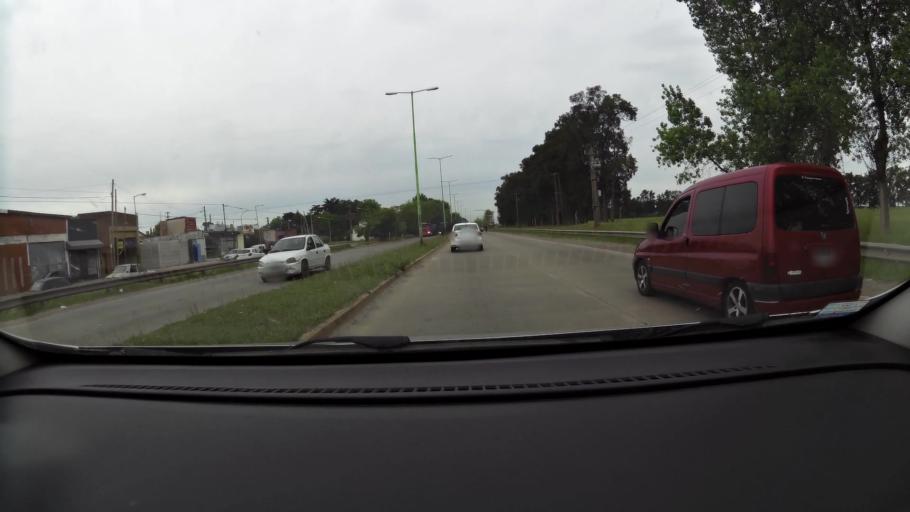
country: AR
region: Buenos Aires
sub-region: Partido de Campana
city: Campana
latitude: -34.1792
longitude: -58.9427
